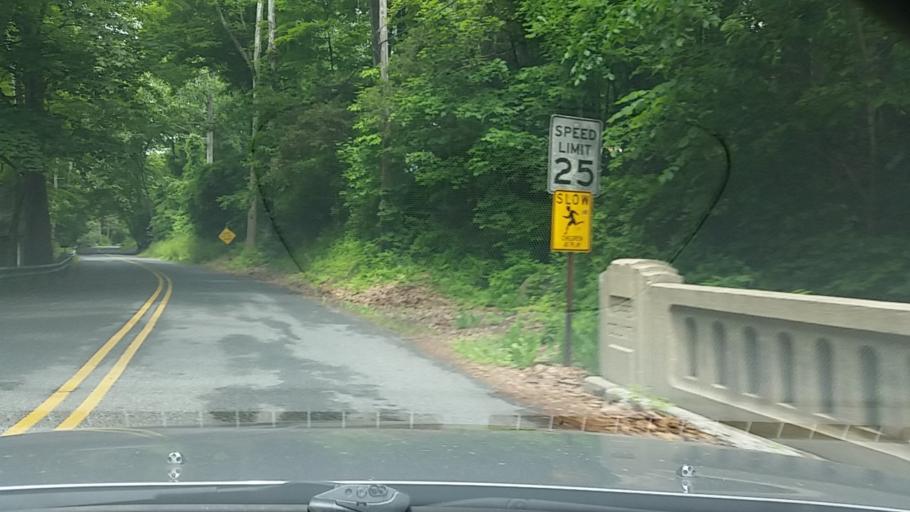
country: US
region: New Jersey
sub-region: Warren County
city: Oxford
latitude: 40.8603
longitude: -74.9769
